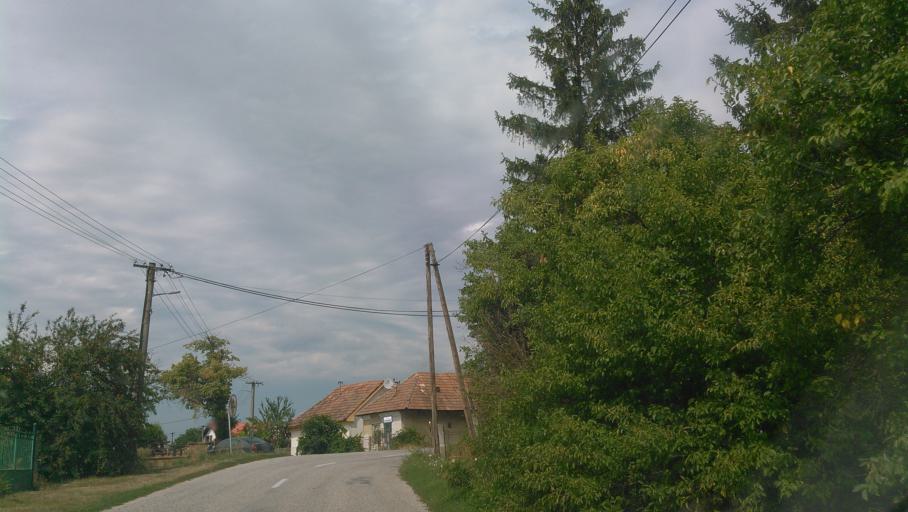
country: SK
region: Trnavsky
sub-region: Okres Trnava
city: Piestany
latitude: 48.5017
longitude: 17.9849
